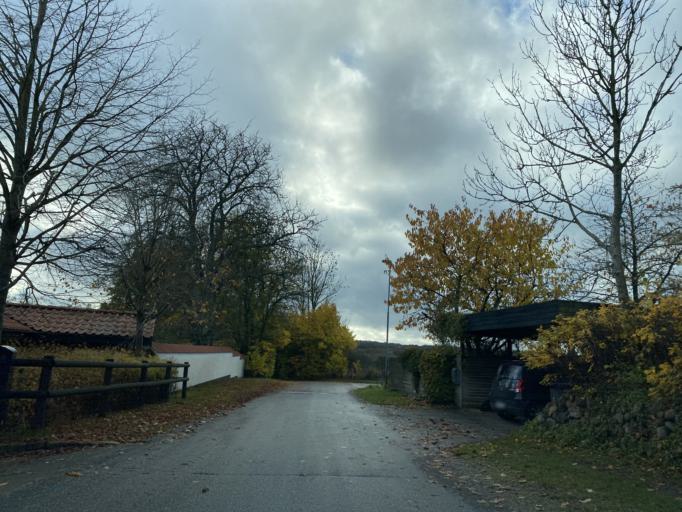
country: DK
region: Central Jutland
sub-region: Skanderborg Kommune
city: Skovby
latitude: 56.2232
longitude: 9.9576
